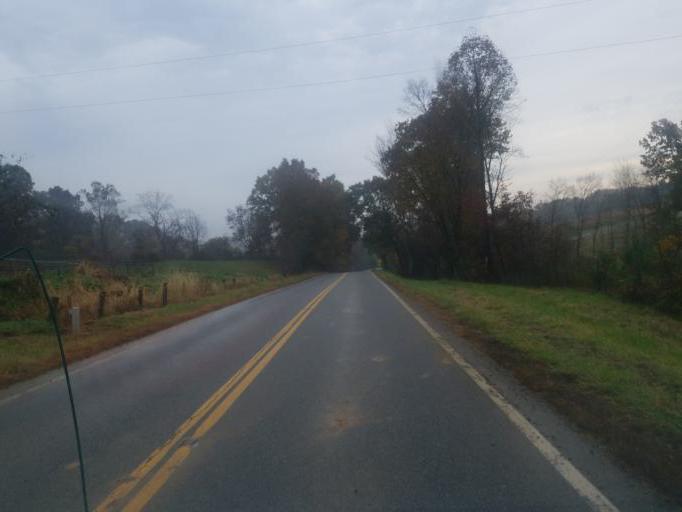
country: US
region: Ohio
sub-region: Morgan County
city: McConnelsville
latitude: 39.4731
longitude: -81.8837
